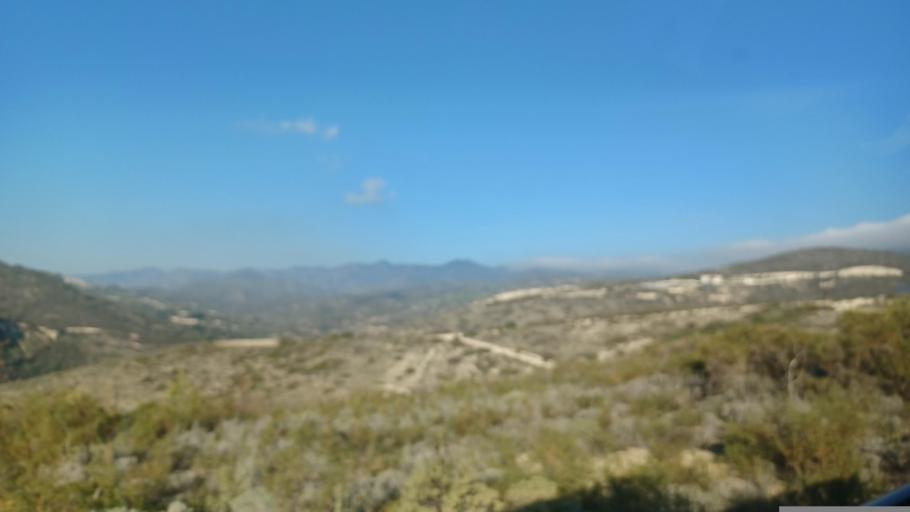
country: CY
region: Larnaka
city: Kofinou
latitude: 34.8354
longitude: 33.3025
